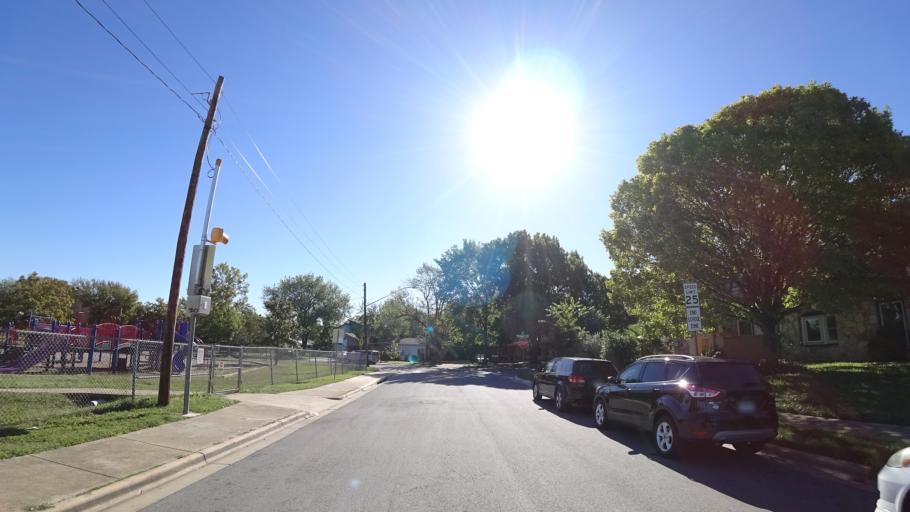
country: US
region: Texas
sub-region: Travis County
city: Austin
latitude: 30.2331
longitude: -97.7632
